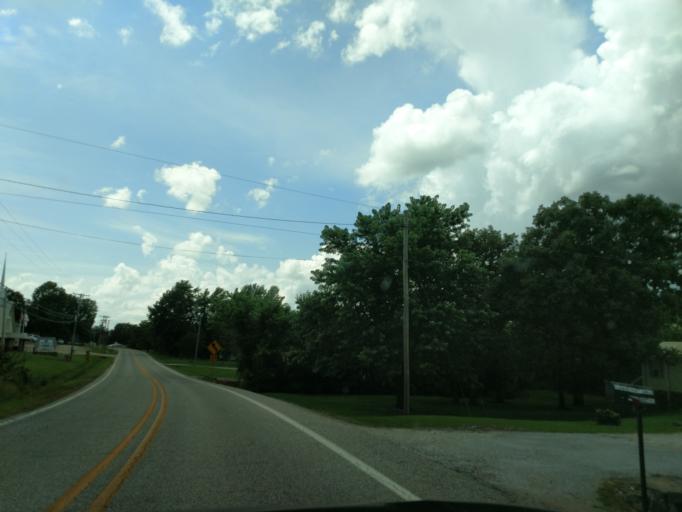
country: US
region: Arkansas
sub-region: Boone County
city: Harrison
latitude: 36.2504
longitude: -93.2154
